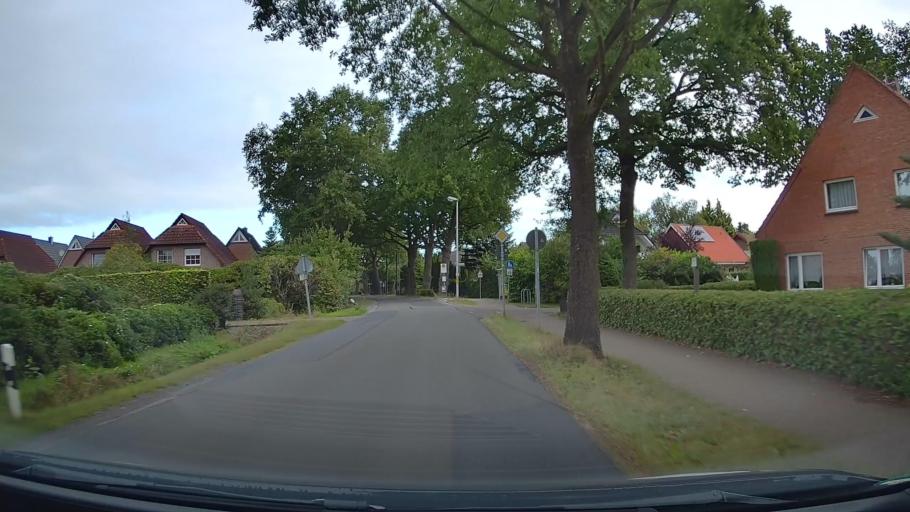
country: DE
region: Lower Saxony
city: Oldenburg
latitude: 53.1341
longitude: 8.1455
